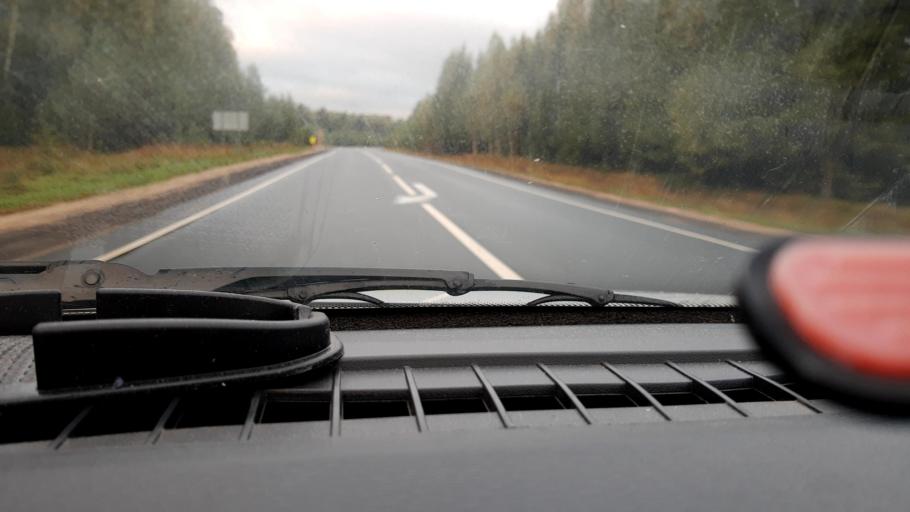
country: RU
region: Nizjnij Novgorod
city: Linda
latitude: 56.6982
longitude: 44.2107
